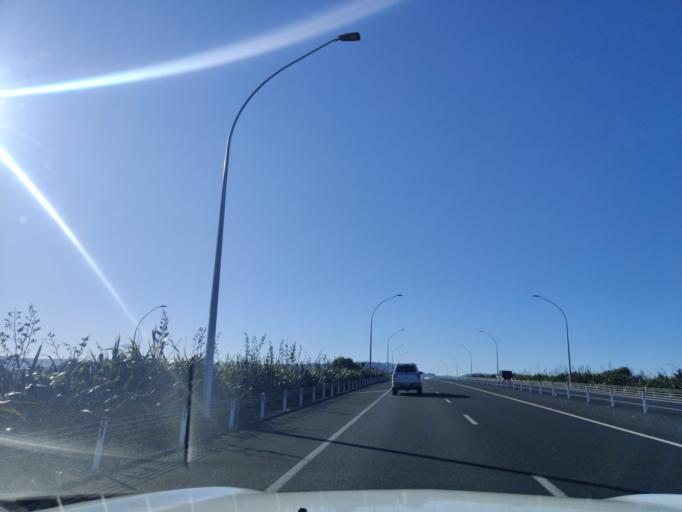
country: NZ
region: Waikato
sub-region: Waipa District
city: Cambridge
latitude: -37.8683
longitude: 175.4546
